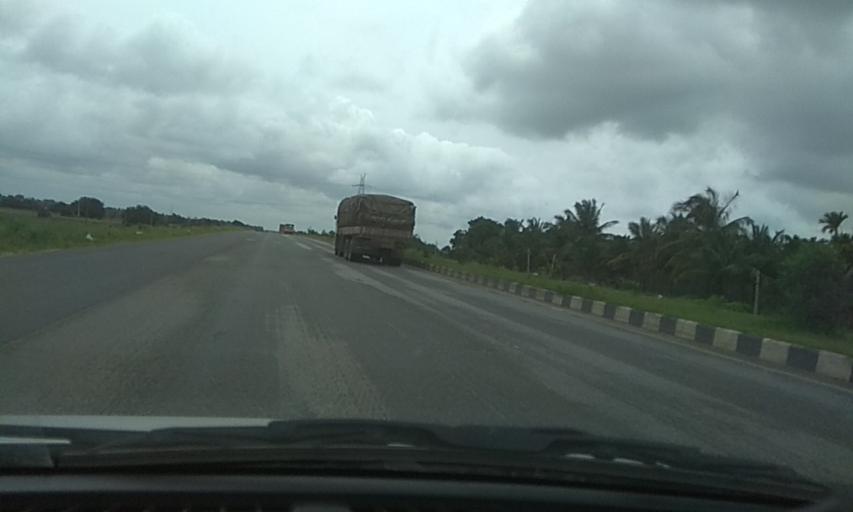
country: IN
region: Karnataka
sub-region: Davanagere
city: Mayakonda
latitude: 14.3699
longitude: 76.1329
